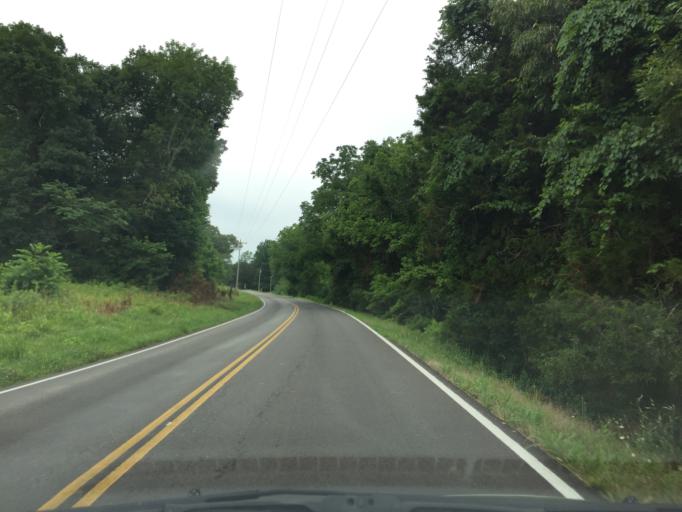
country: US
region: Tennessee
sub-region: Bradley County
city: Hopewell
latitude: 35.3800
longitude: -84.8867
